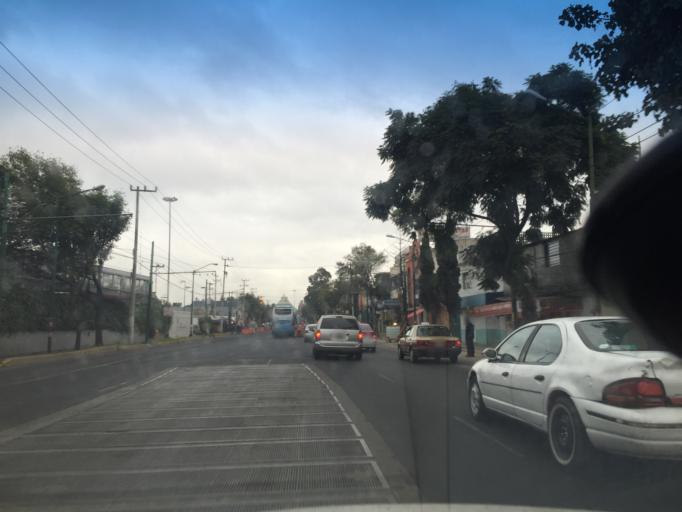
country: MX
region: Mexico City
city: Gustavo A. Madero
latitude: 19.4831
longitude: -99.1087
